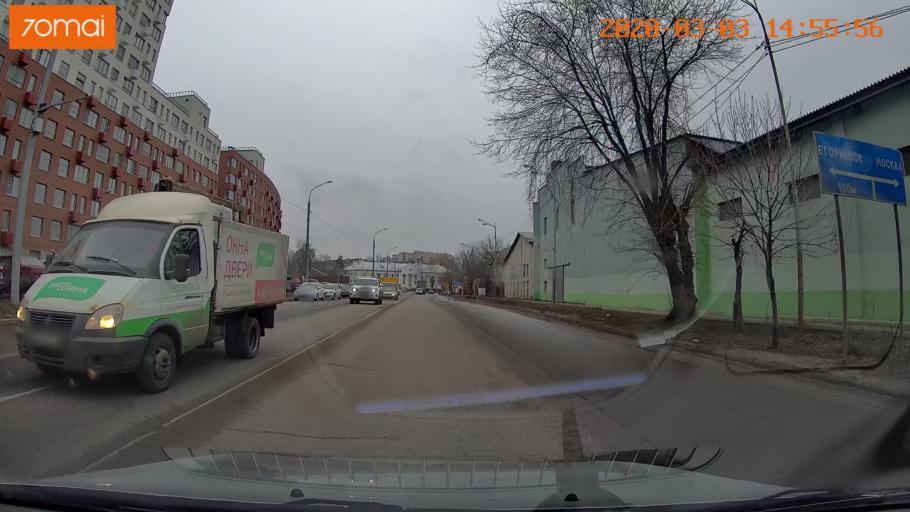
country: RU
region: Moskovskaya
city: Korenevo
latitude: 55.6642
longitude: 37.9973
